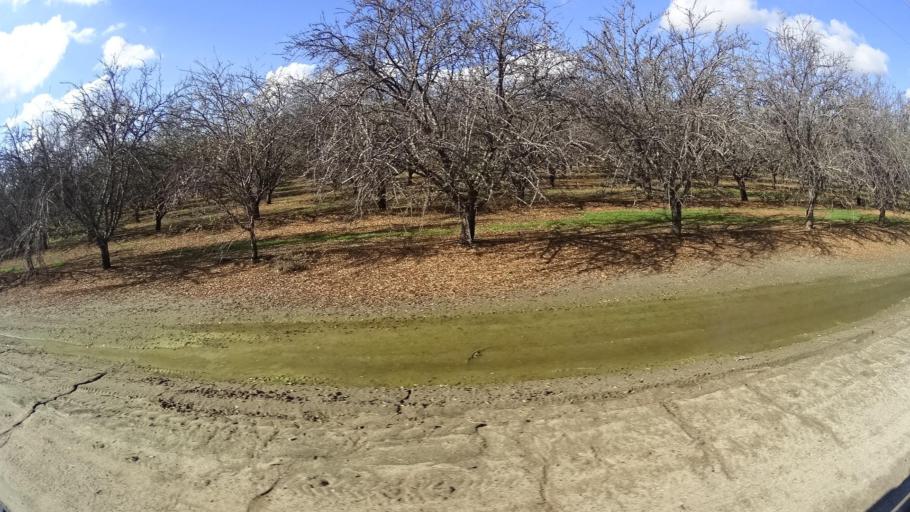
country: US
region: California
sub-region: Kern County
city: McFarland
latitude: 35.6593
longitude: -119.2411
